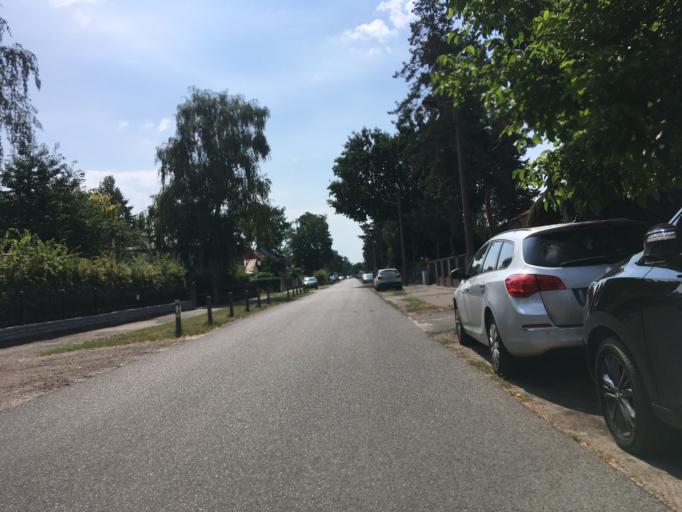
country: DE
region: Berlin
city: Mahlsdorf
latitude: 52.4807
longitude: 13.6103
